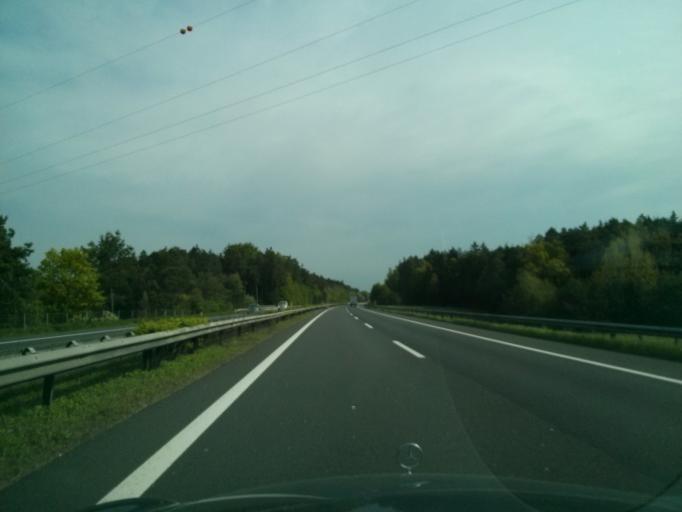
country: AT
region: Styria
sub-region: Politischer Bezirk Hartberg-Fuerstenfeld
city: Bad Waltersdorf
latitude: 47.1406
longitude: 15.9899
